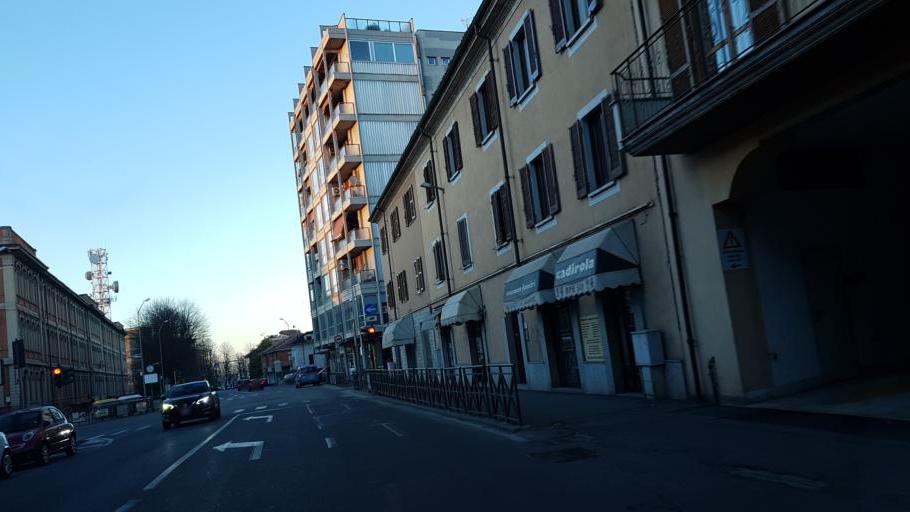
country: IT
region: Piedmont
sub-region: Provincia di Alessandria
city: Tortona
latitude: 44.8959
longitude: 8.8623
